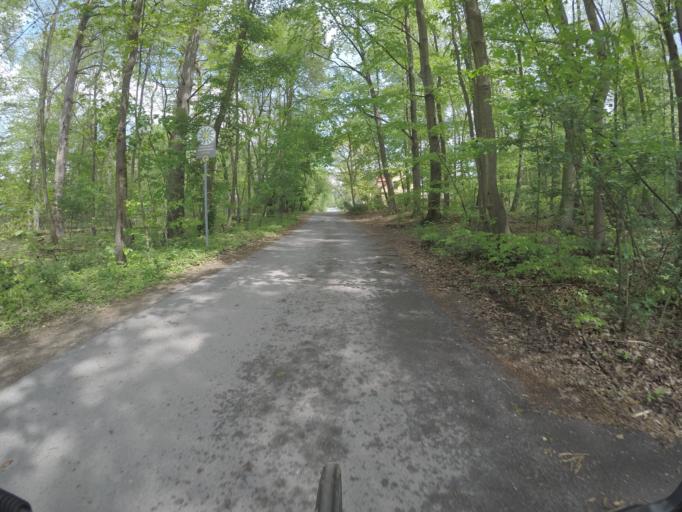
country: DE
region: Brandenburg
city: Joachimsthal
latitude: 52.9641
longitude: 13.7446
